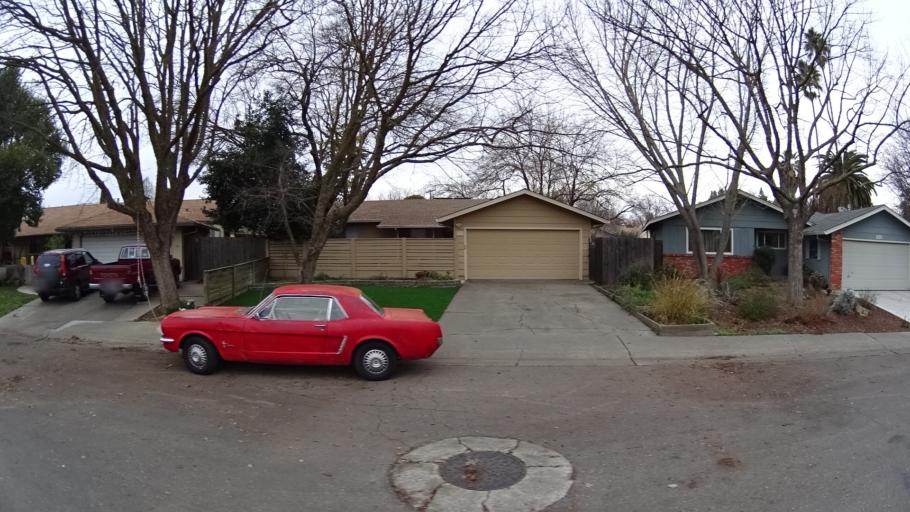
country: US
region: California
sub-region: Yolo County
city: Davis
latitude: 38.5609
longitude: -121.7197
